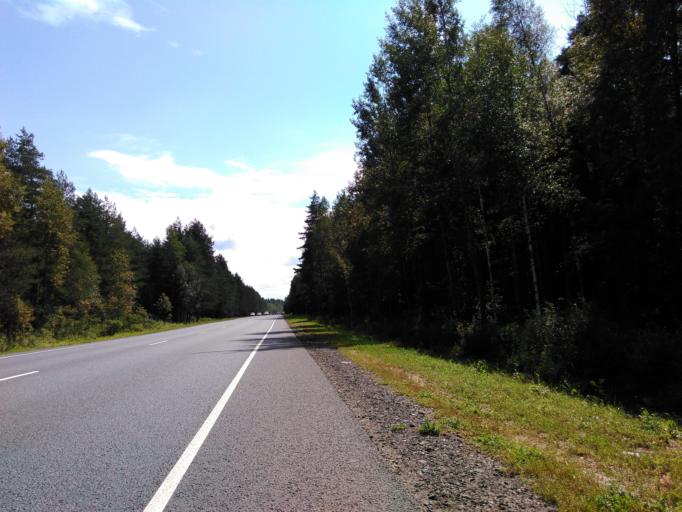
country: RU
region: Moskovskaya
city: Elektrogorsk
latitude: 56.0305
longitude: 38.7525
